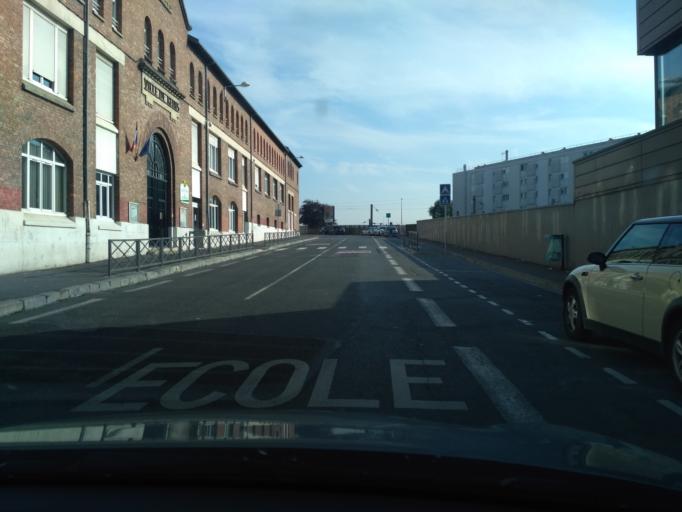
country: FR
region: Champagne-Ardenne
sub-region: Departement de la Marne
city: Reims
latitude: 49.2622
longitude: 4.0265
